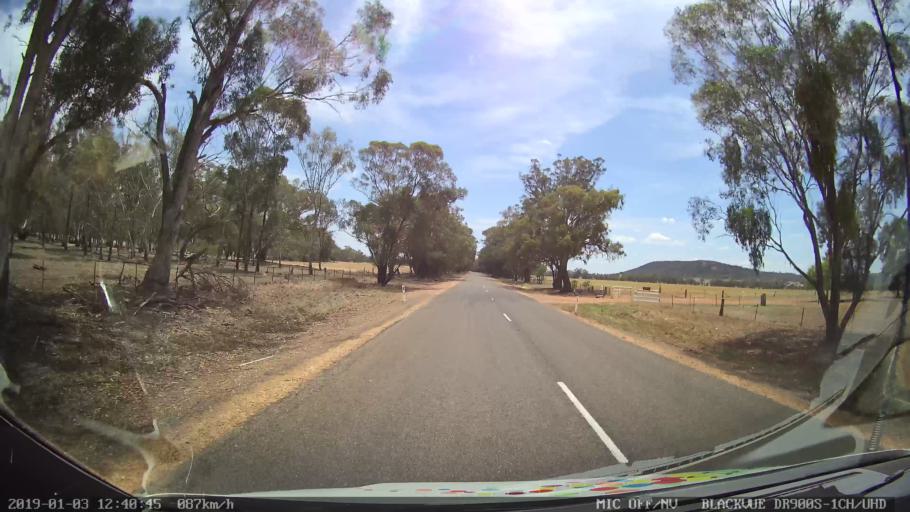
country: AU
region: New South Wales
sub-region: Weddin
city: Grenfell
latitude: -33.8086
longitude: 148.2135
